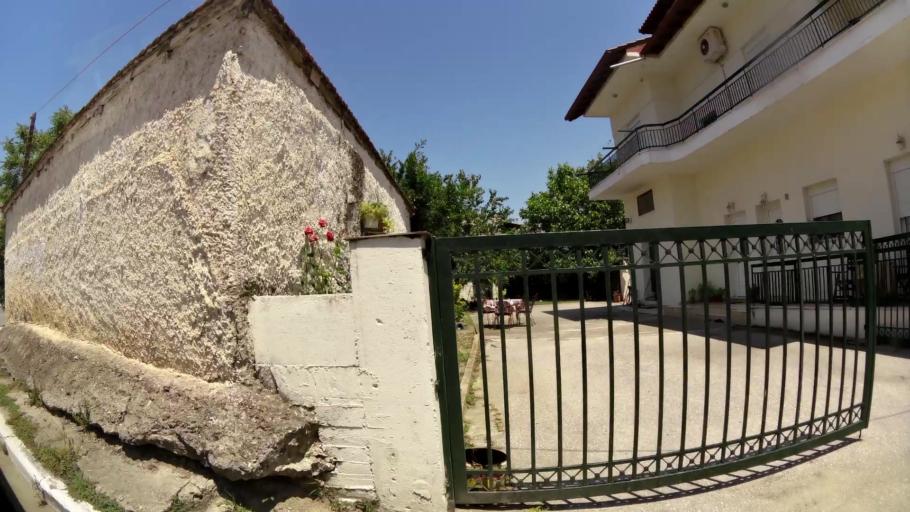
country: GR
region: Central Macedonia
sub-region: Nomos Thessalonikis
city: Epanomi
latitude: 40.4306
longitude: 22.9281
